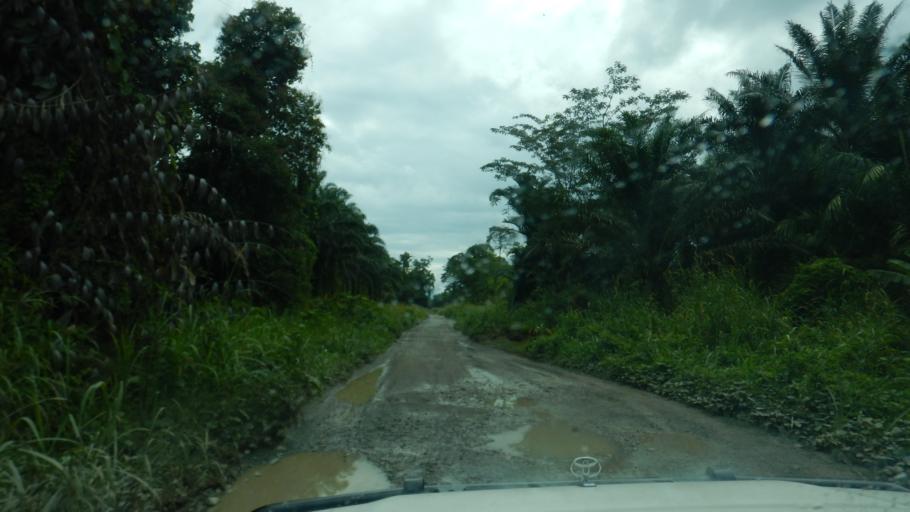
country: PG
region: Northern Province
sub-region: Sohe
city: Kokoda
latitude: -8.9177
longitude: 147.9414
